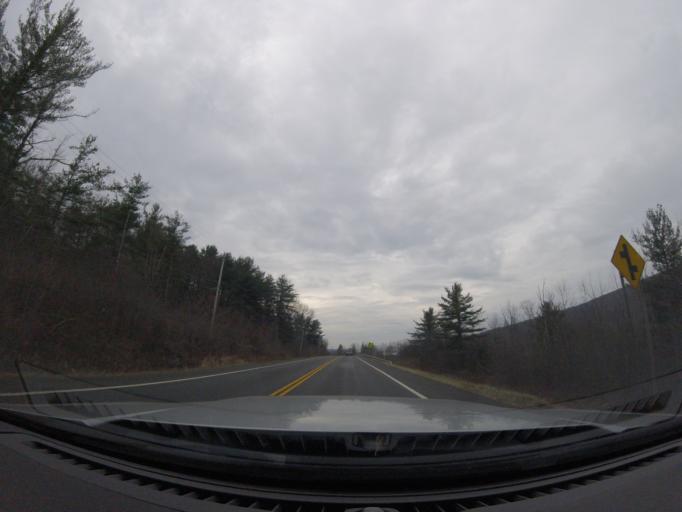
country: US
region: New York
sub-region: Schuyler County
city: Watkins Glen
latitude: 42.4414
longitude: -76.7907
